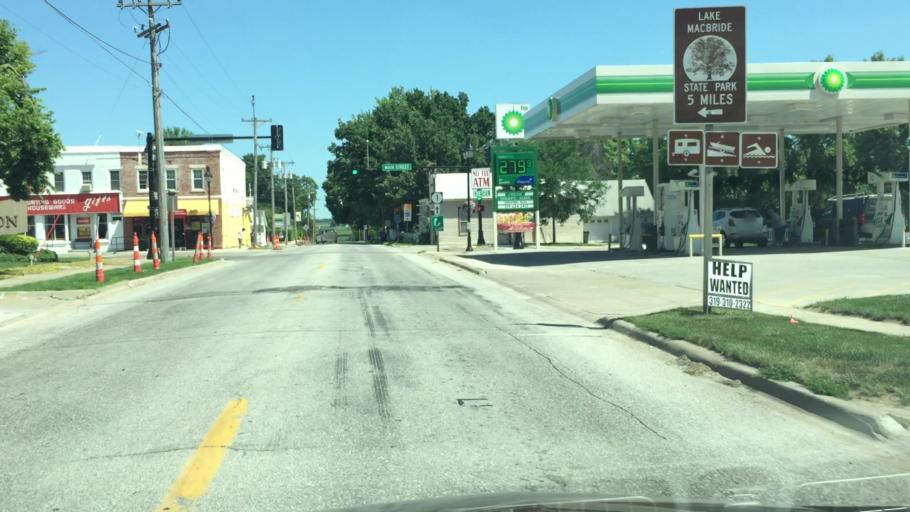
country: US
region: Iowa
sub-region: Johnson County
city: Solon
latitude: 41.8067
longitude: -91.4930
